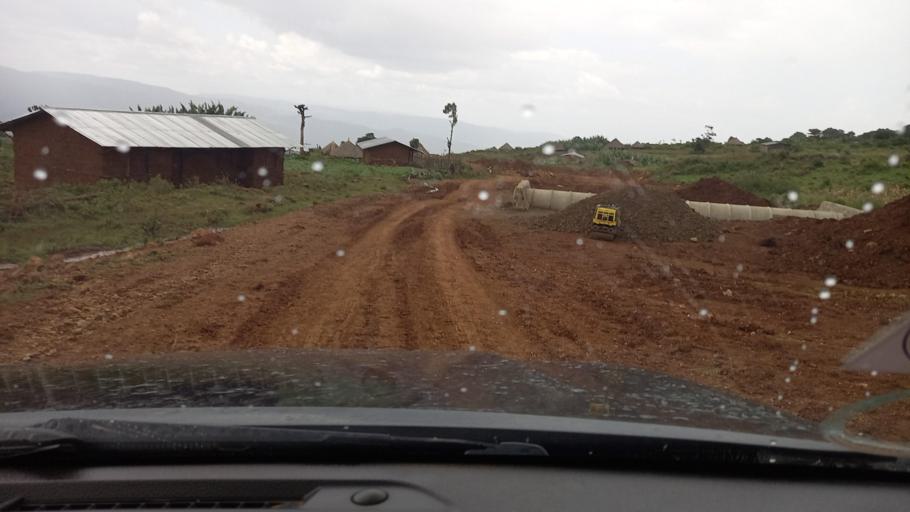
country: ET
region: Southern Nations, Nationalities, and People's Region
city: Mizan Teferi
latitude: 6.1639
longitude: 35.7261
